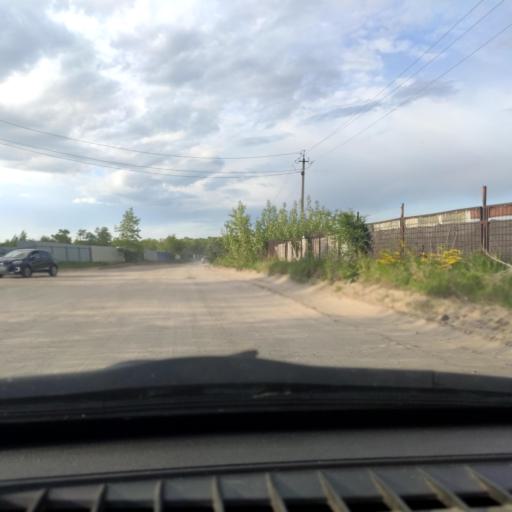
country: RU
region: Samara
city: Zhigulevsk
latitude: 53.4525
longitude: 49.5348
